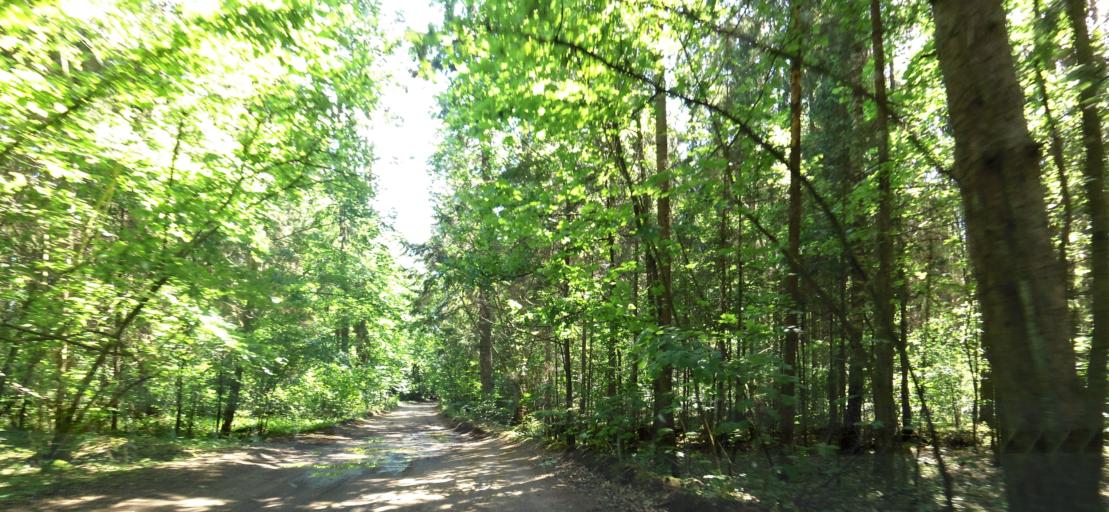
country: LT
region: Vilnius County
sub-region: Vilnius
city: Fabijoniskes
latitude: 54.8272
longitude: 25.3206
